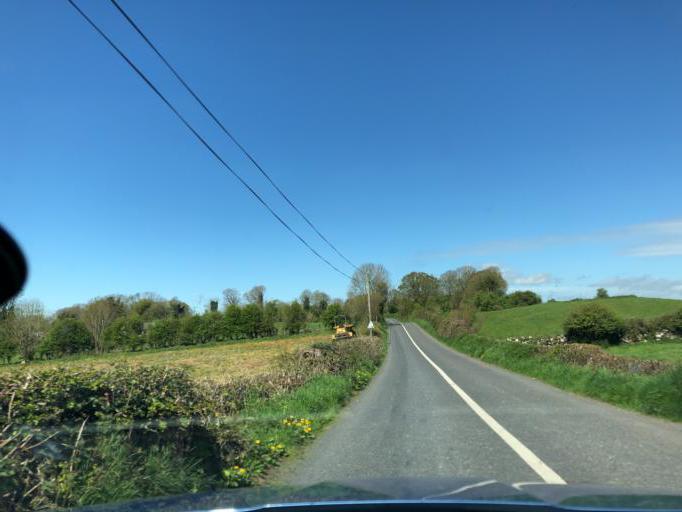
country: IE
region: Connaught
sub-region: County Galway
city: Loughrea
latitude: 53.1617
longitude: -8.3994
